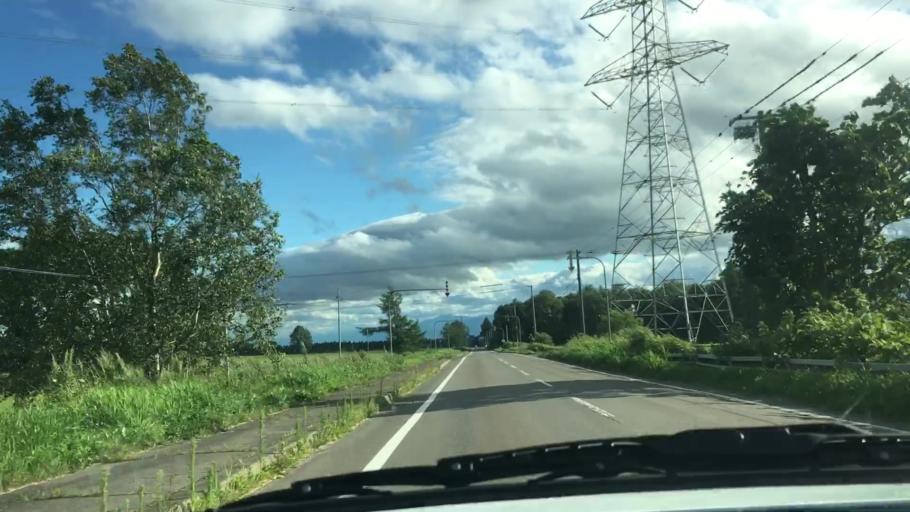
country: JP
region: Hokkaido
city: Otofuke
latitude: 43.1750
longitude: 143.0067
